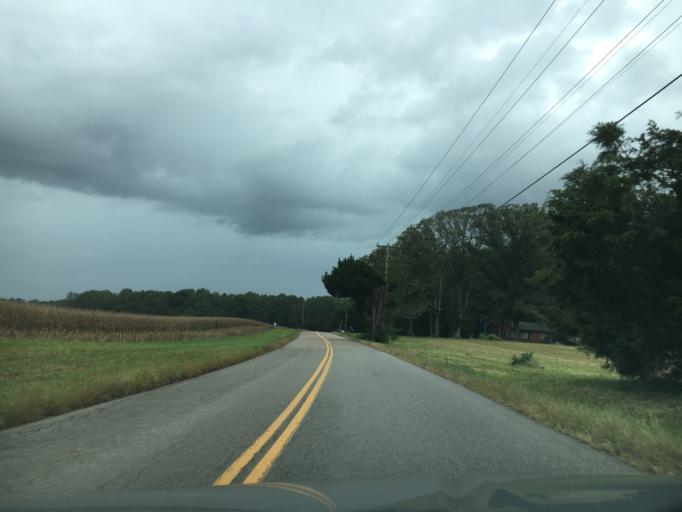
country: US
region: Virginia
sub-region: Amelia County
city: Amelia Court House
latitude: 37.3608
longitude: -77.9742
